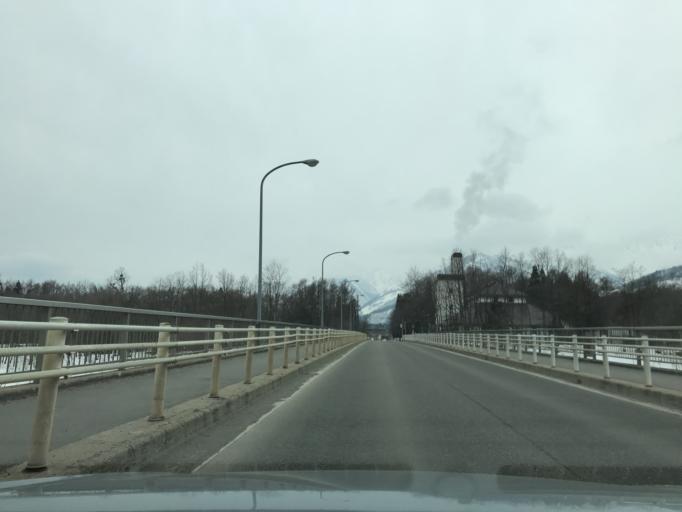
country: JP
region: Nagano
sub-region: Kitaazumi Gun
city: Hakuba
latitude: 36.7083
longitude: 137.8467
